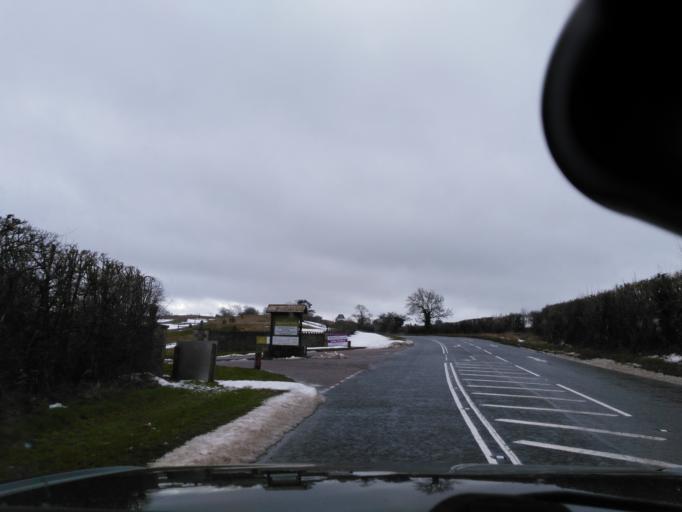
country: GB
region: England
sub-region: Wiltshire
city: Bradford-on-Avon
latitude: 51.3641
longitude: -2.2648
